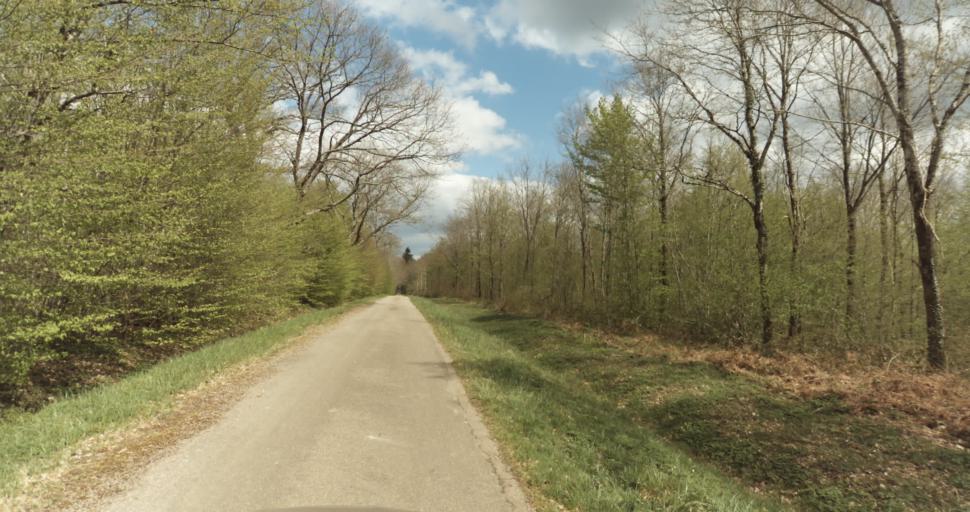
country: FR
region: Franche-Comte
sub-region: Departement du Jura
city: Champvans
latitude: 47.1584
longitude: 5.4368
